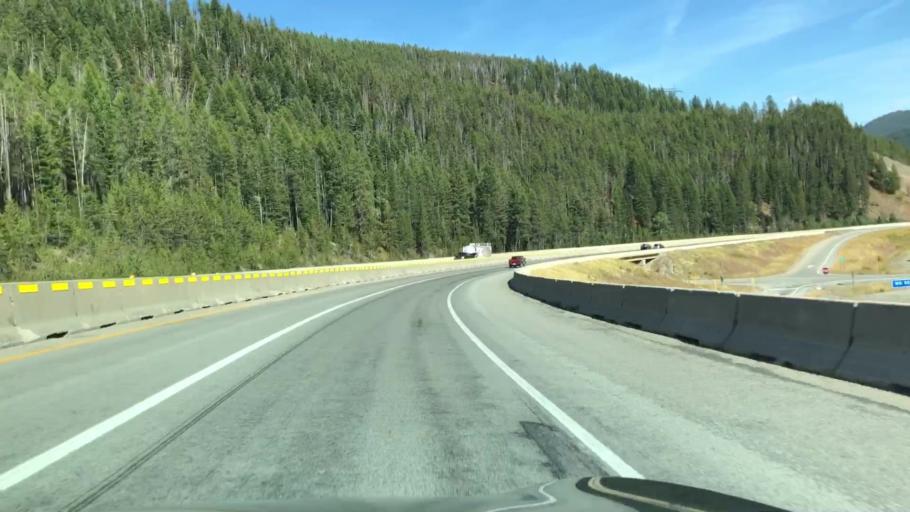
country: US
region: Montana
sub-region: Sanders County
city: Thompson Falls
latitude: 47.4219
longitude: -115.6091
